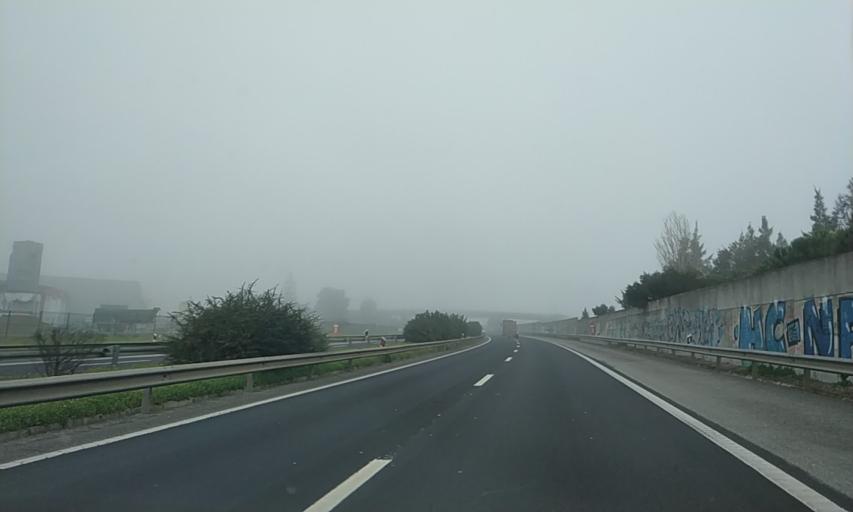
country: PT
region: Setubal
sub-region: Montijo
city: Montijo
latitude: 38.6908
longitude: -8.9389
